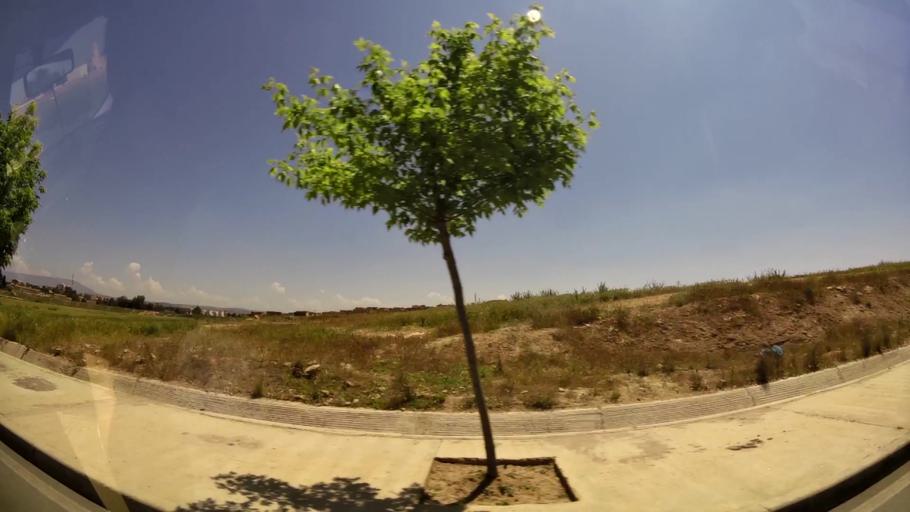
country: MA
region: Oriental
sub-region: Oujda-Angad
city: Oujda
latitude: 34.6946
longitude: -1.9278
